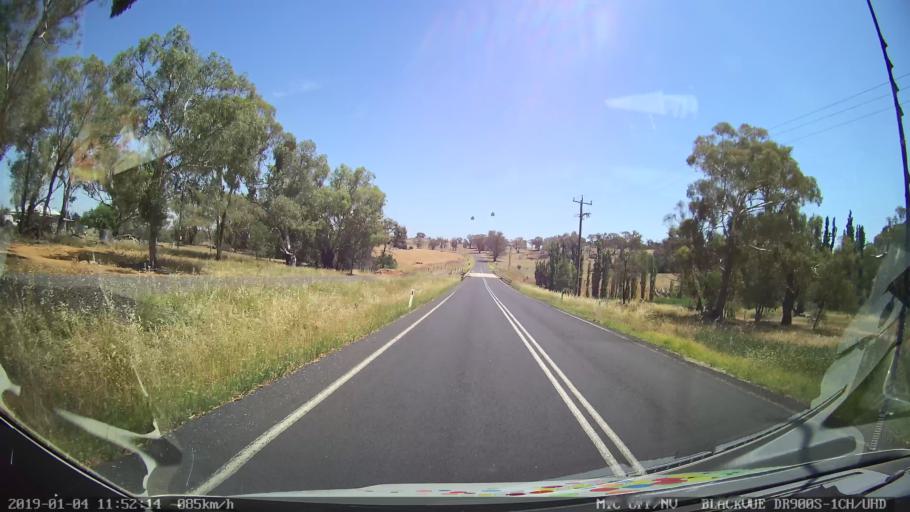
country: AU
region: New South Wales
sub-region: Cabonne
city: Molong
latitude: -32.8860
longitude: 148.7504
